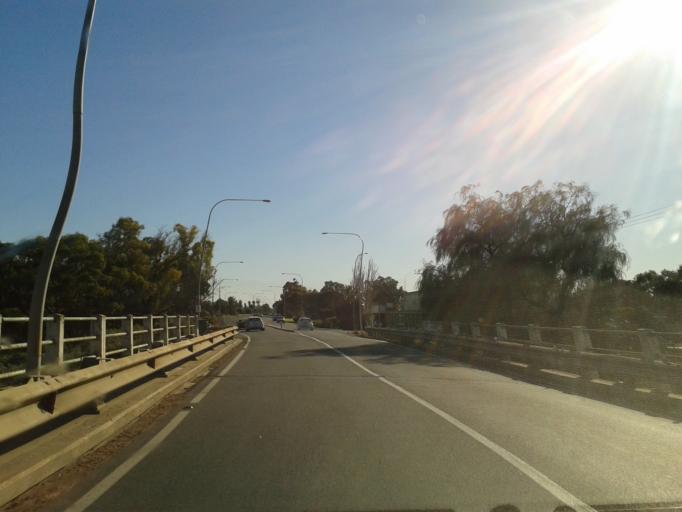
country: AU
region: South Australia
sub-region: Renmark Paringa
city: Renmark
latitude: -34.1872
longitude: 140.7296
